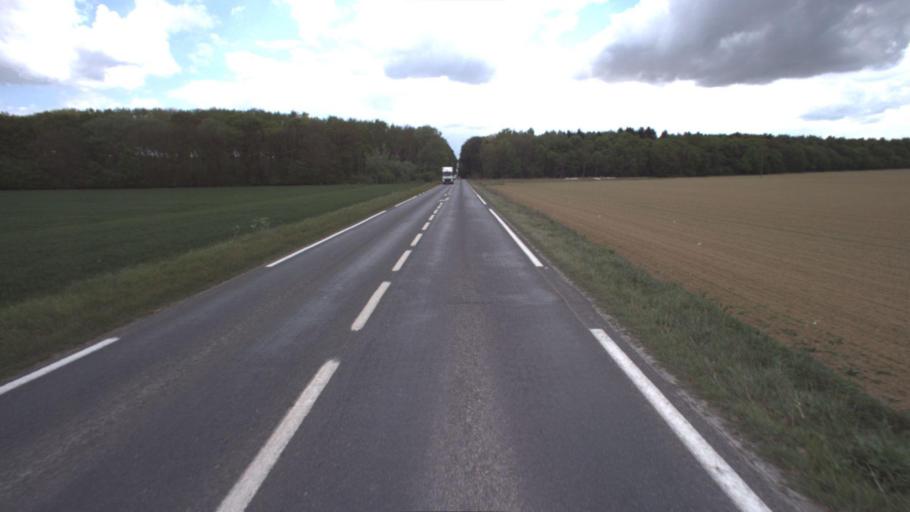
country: FR
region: Ile-de-France
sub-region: Departement de Seine-et-Marne
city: Saint-Pathus
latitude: 49.0614
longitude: 2.7784
